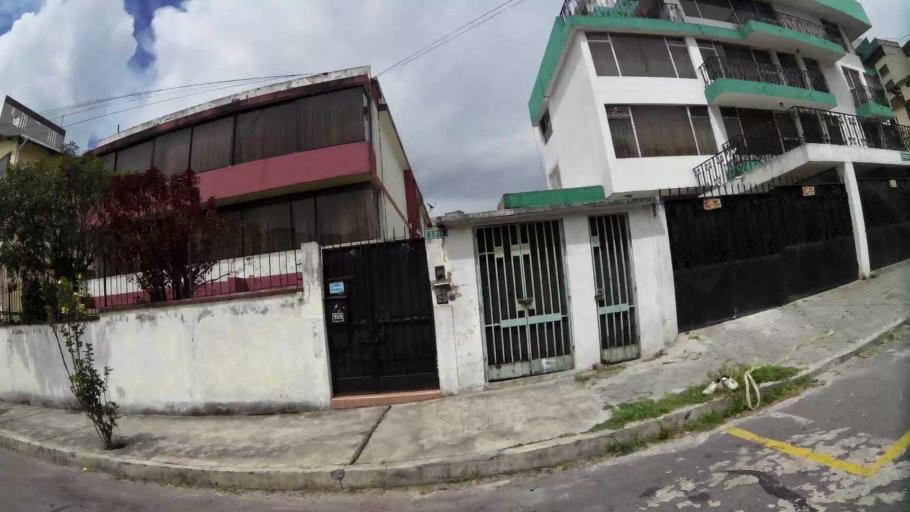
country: EC
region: Pichincha
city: Quito
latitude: -0.1855
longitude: -78.4900
